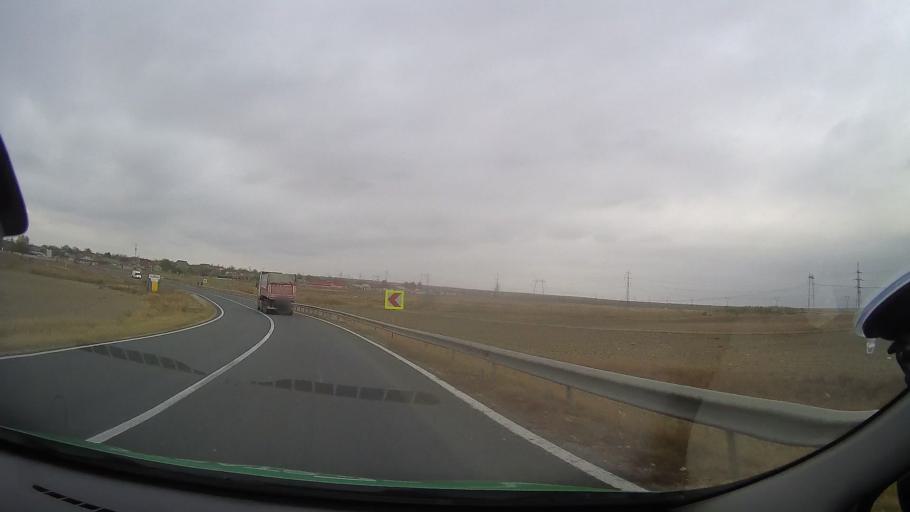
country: RO
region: Constanta
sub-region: Comuna Castelu
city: Castelu
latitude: 44.2586
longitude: 28.3480
